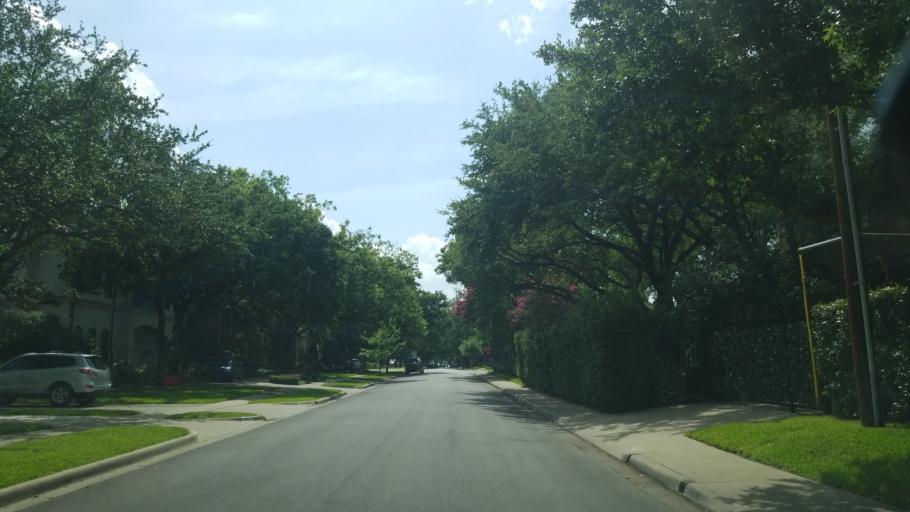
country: US
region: Texas
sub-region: Dallas County
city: University Park
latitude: 32.8530
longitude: -96.7929
